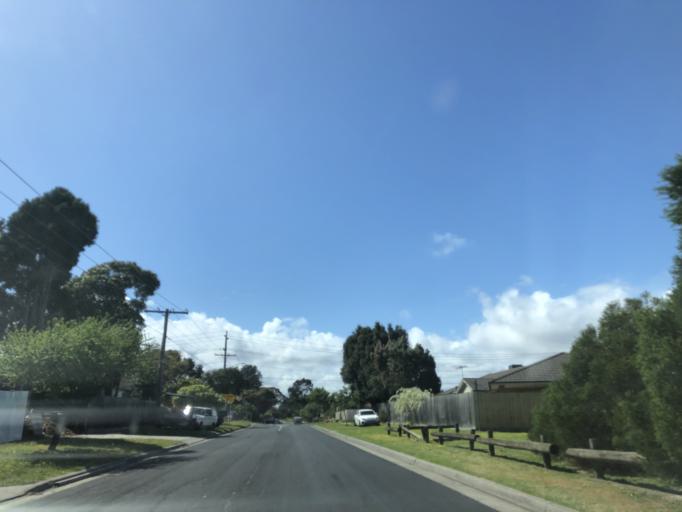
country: AU
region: Victoria
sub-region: Monash
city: Oakleigh South
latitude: -37.9309
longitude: 145.1024
